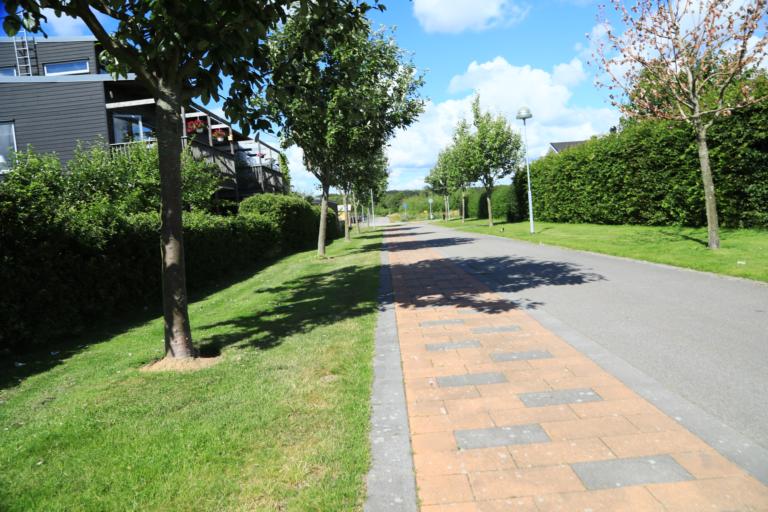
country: SE
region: Halland
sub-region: Varbergs Kommun
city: Traslovslage
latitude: 57.0873
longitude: 12.2796
